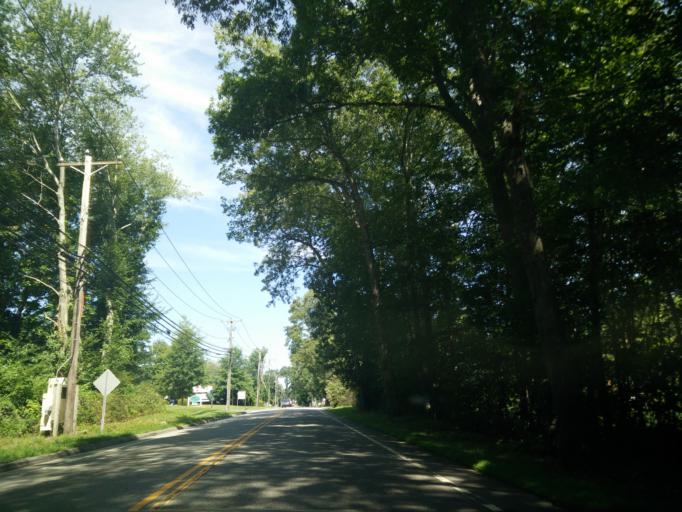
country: US
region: Connecticut
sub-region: Middlesex County
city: Clinton
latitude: 41.3486
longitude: -72.5603
